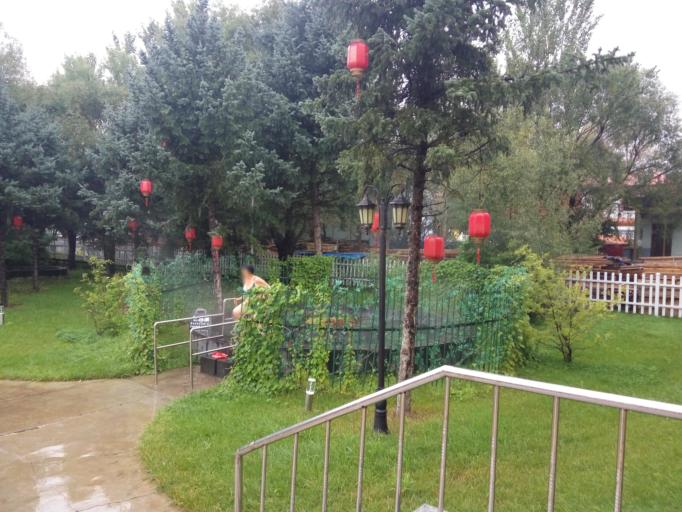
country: CN
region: Heilongjiang Sheng
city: Erjing
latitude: 48.6508
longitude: 126.1403
